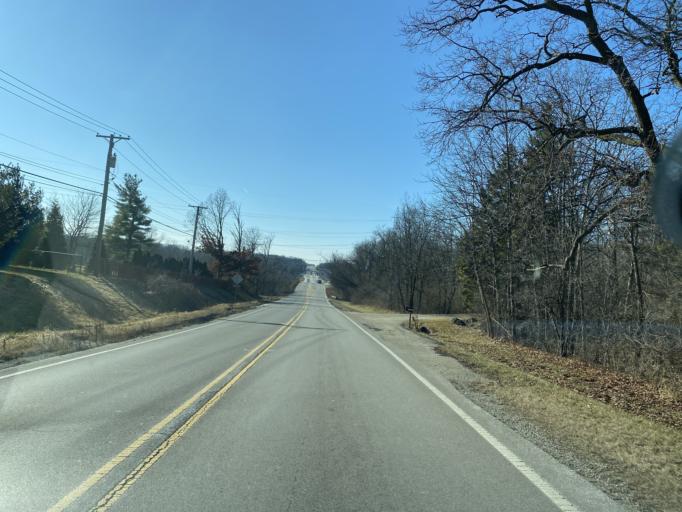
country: US
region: Illinois
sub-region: Cook County
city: Lemont
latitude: 41.6471
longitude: -87.9963
